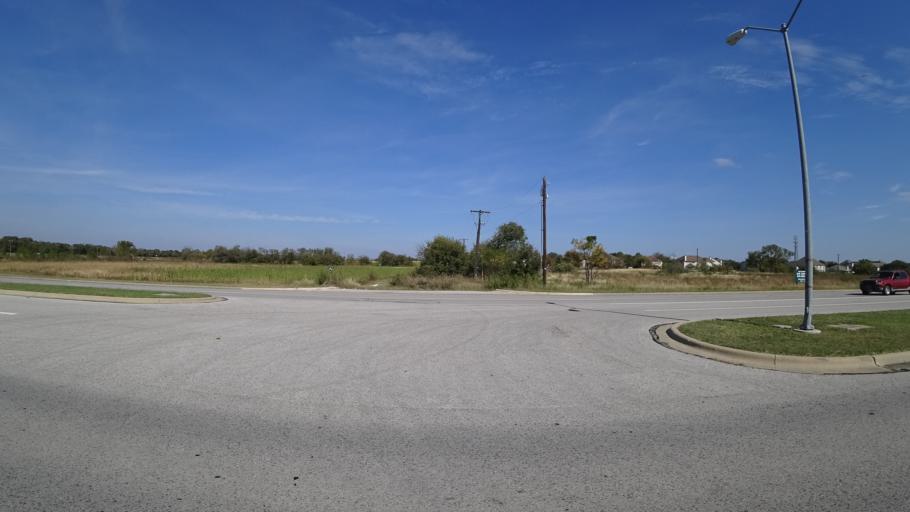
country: US
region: Texas
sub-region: Travis County
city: Pflugerville
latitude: 30.4234
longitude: -97.6238
